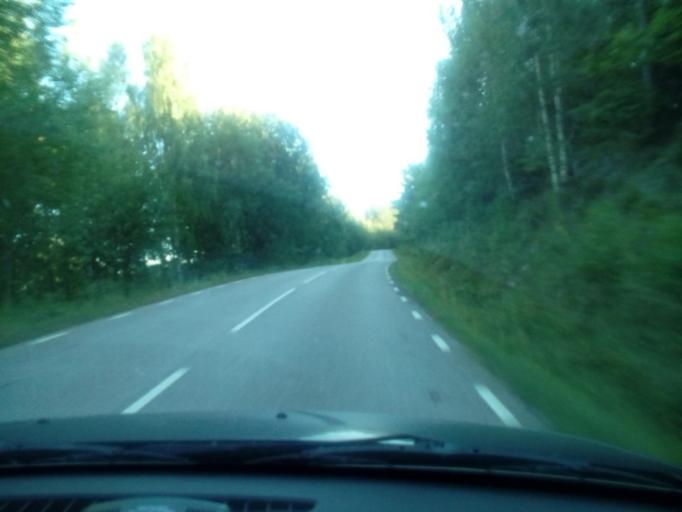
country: SE
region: Kalmar
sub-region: Vasterviks Kommun
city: Gamleby
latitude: 57.8105
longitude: 16.4351
